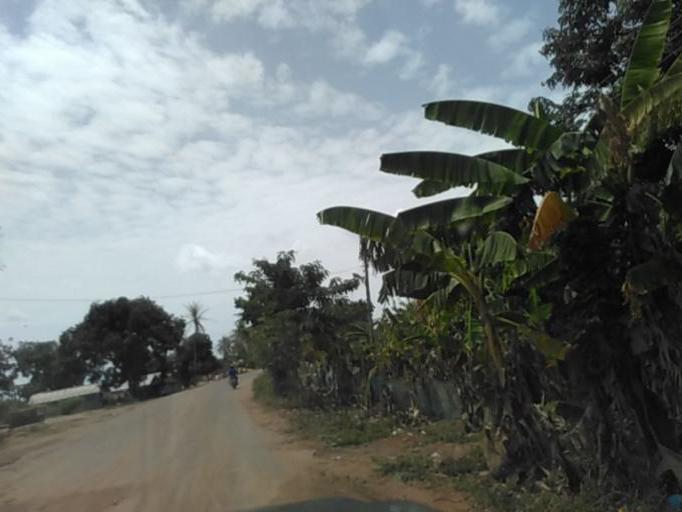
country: GH
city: Akropong
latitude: 6.0963
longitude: 0.1649
